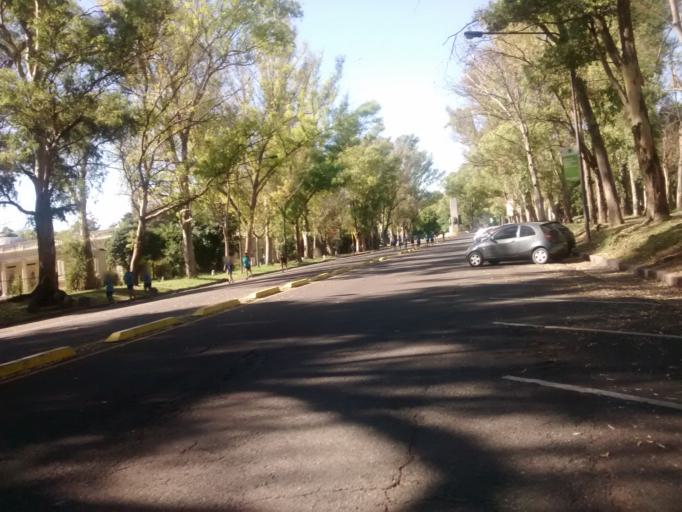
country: AR
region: Buenos Aires
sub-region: Partido de La Plata
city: La Plata
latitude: -34.9075
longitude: -57.9337
